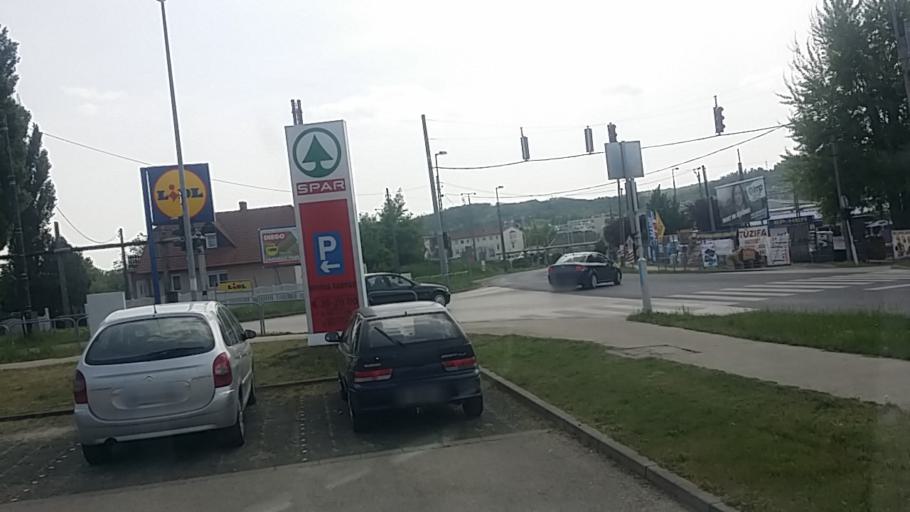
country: HU
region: Komarom-Esztergom
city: Dorog
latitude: 47.7297
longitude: 18.7259
